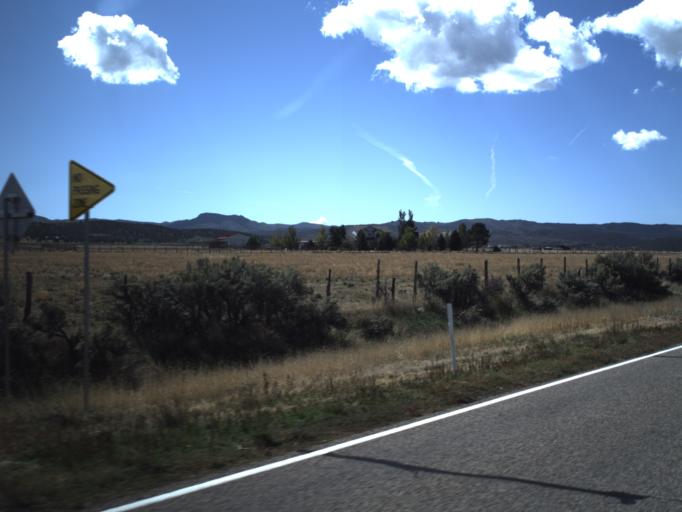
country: US
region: Utah
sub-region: Washington County
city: Enterprise
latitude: 37.5773
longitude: -113.6956
